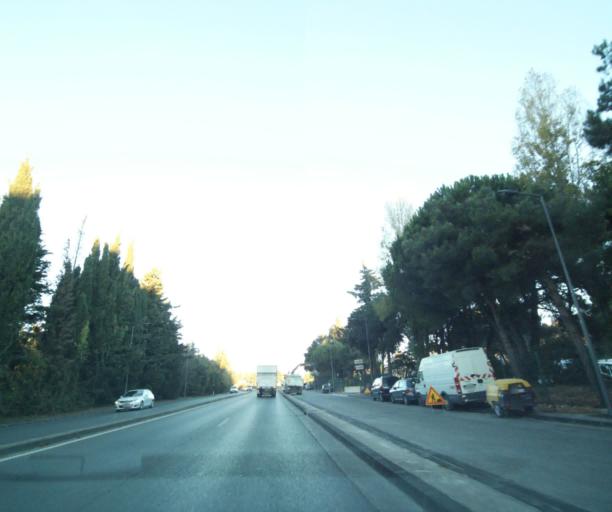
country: FR
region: Provence-Alpes-Cote d'Azur
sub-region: Departement des Bouches-du-Rhone
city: Allauch
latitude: 43.3048
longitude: 5.4716
